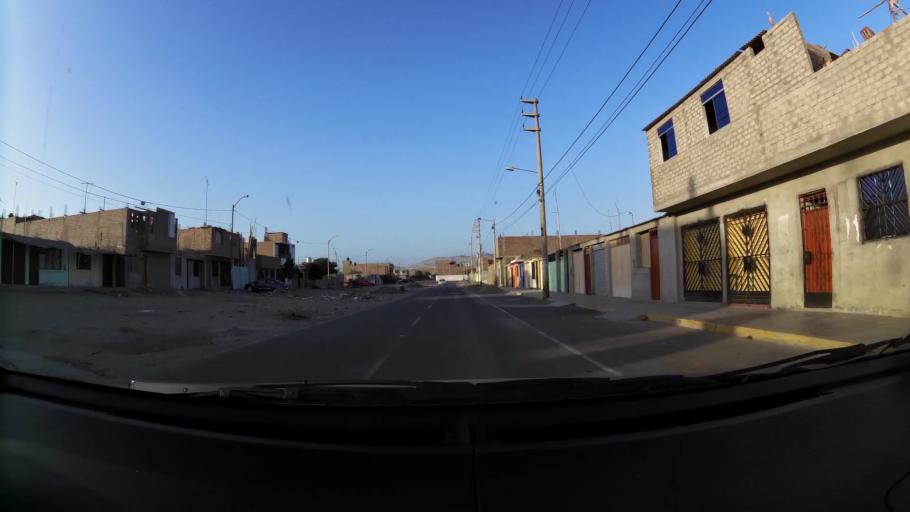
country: PE
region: Ancash
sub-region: Provincia de Santa
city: Buenos Aires
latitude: -9.1456
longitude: -78.5036
